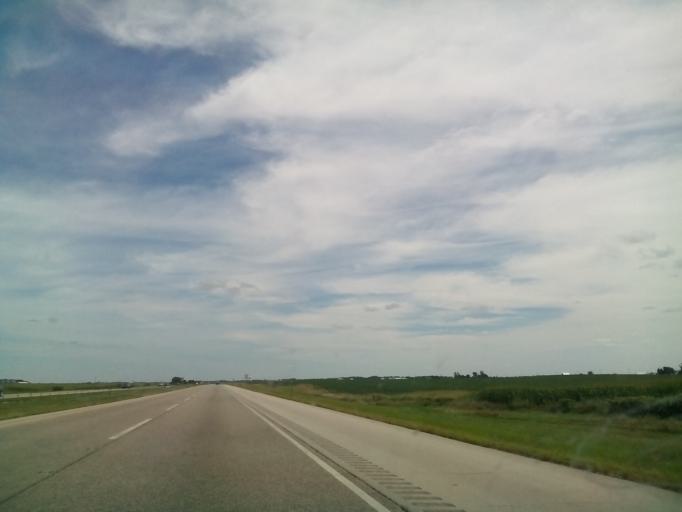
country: US
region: Illinois
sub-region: DeKalb County
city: Malta
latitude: 41.8999
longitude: -88.8342
